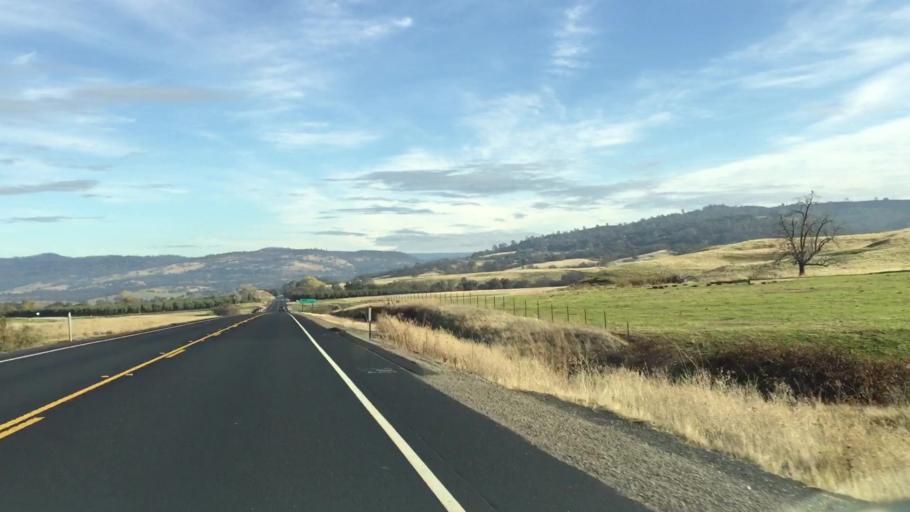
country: US
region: California
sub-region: Butte County
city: Thermalito
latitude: 39.6209
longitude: -121.5981
